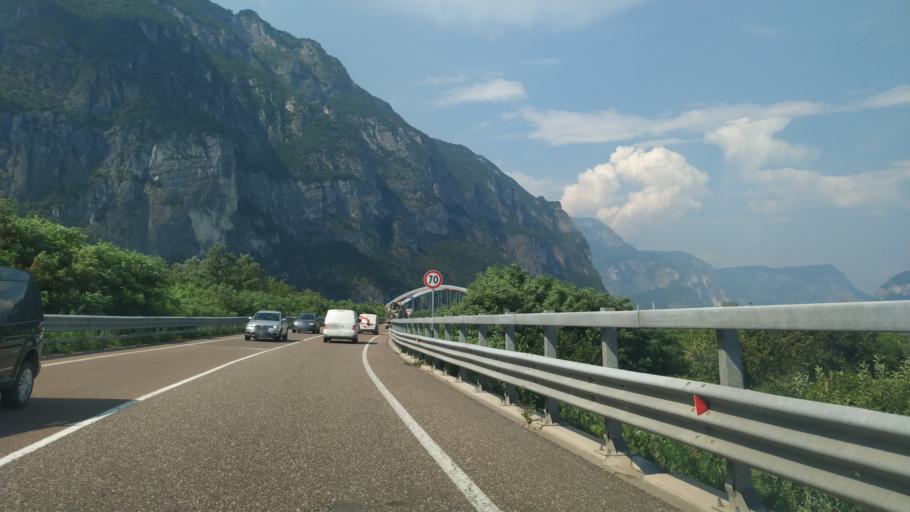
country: IT
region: Trentino-Alto Adige
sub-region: Provincia di Trento
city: Zambana
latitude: 46.1540
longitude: 11.0768
